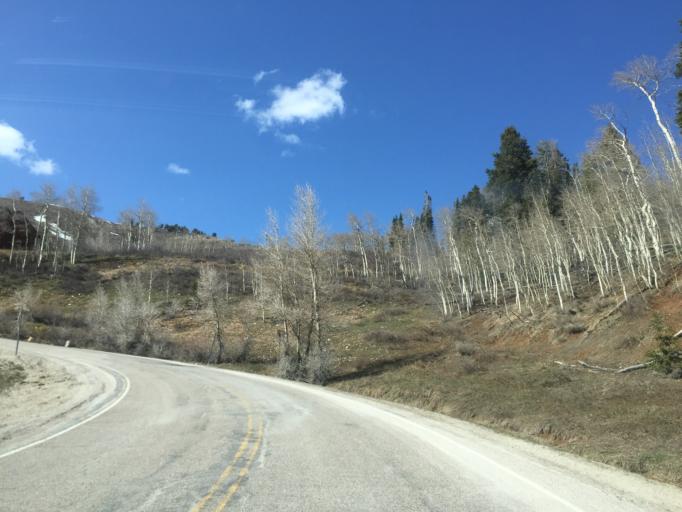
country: US
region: Utah
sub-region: Weber County
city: Wolf Creek
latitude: 41.3767
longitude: -111.7832
